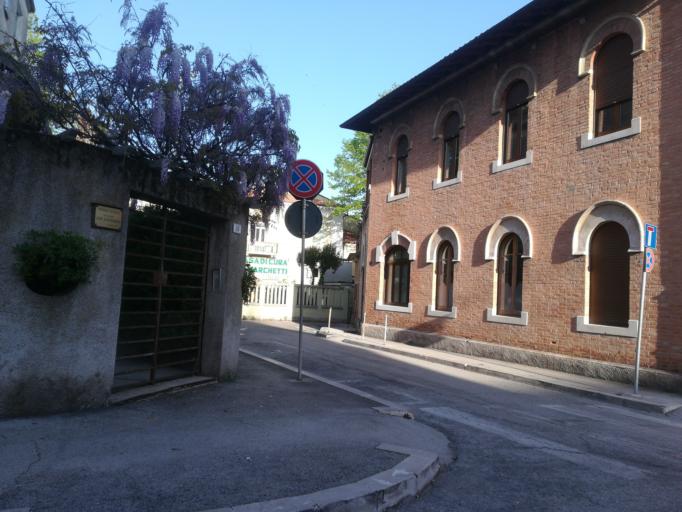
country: IT
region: The Marches
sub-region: Provincia di Macerata
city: Macerata
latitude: 43.2964
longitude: 13.4556
